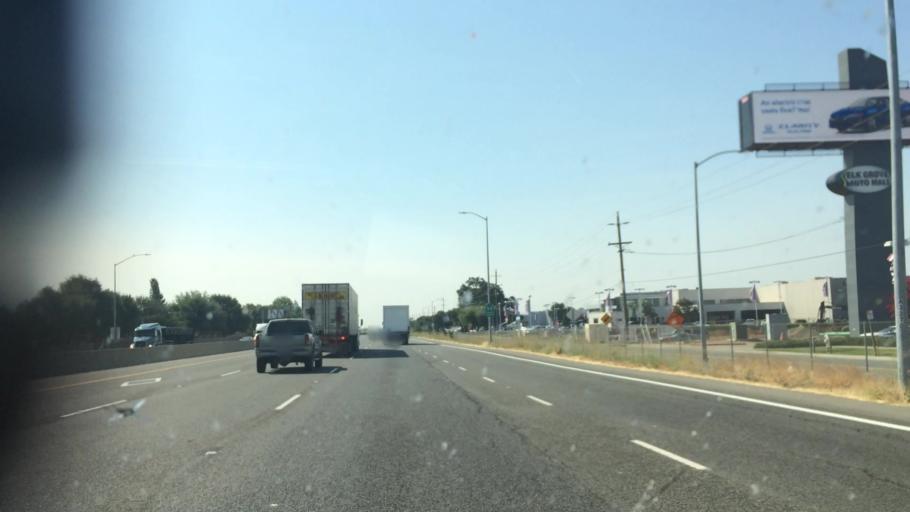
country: US
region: California
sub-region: Sacramento County
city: Elk Grove
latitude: 38.4057
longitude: -121.3867
